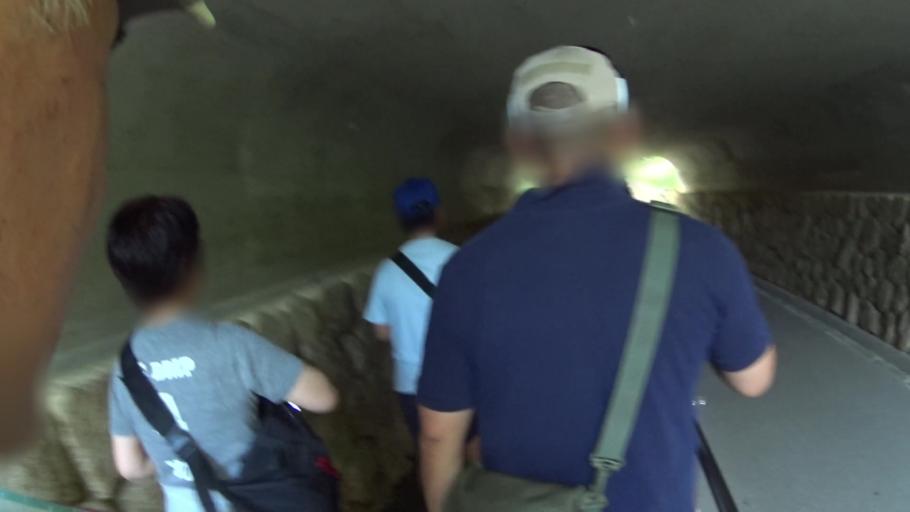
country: JP
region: Nara
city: Kashihara-shi
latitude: 34.4648
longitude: 135.8041
